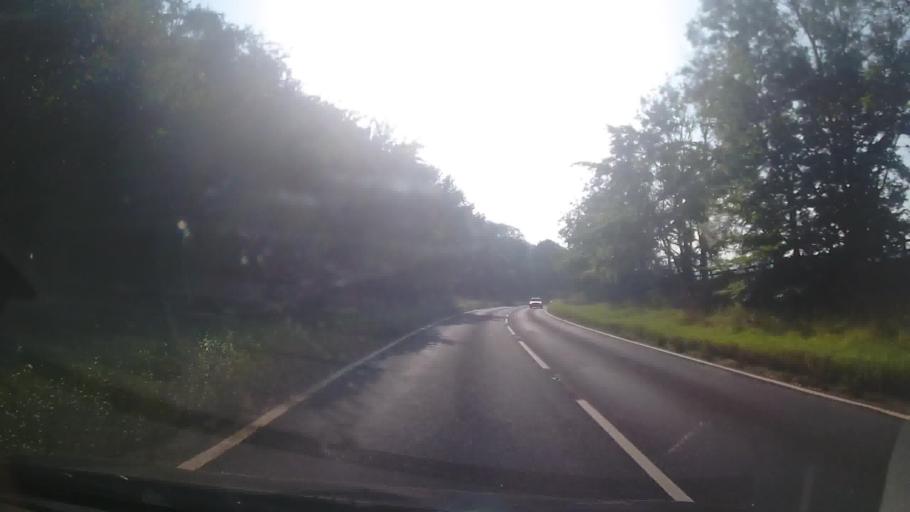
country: GB
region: England
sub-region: Shropshire
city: Much Wenlock
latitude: 52.5748
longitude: -2.5421
